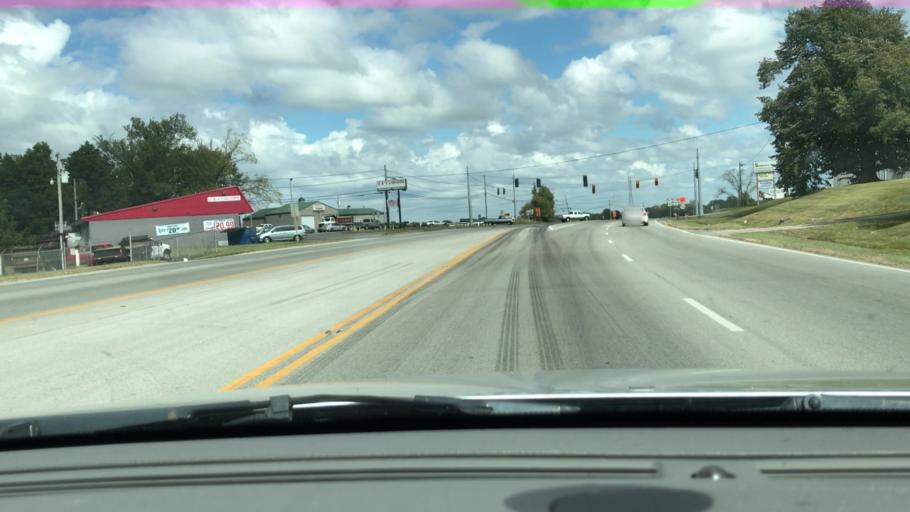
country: US
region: Kentucky
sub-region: Warren County
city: Bowling Green
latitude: 37.0153
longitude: -86.3774
